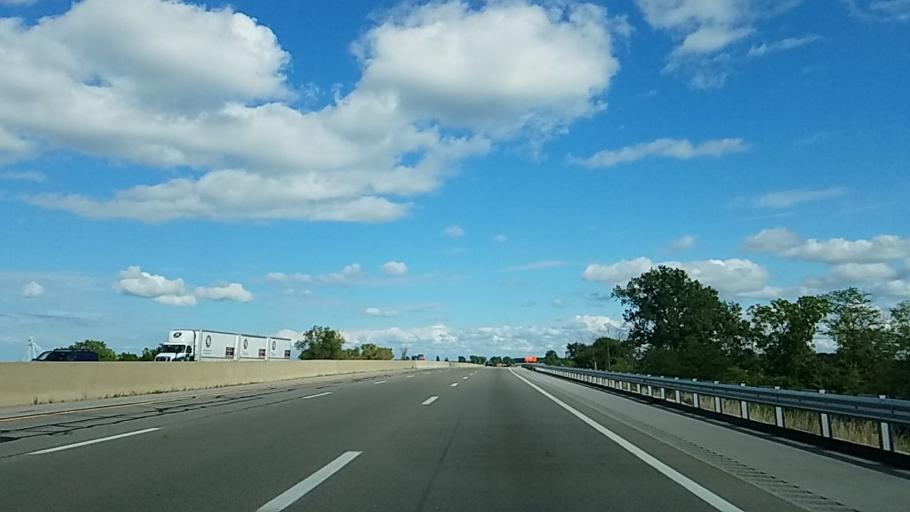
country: US
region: Ohio
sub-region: Sandusky County
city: Clyde
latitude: 41.3577
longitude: -82.8967
